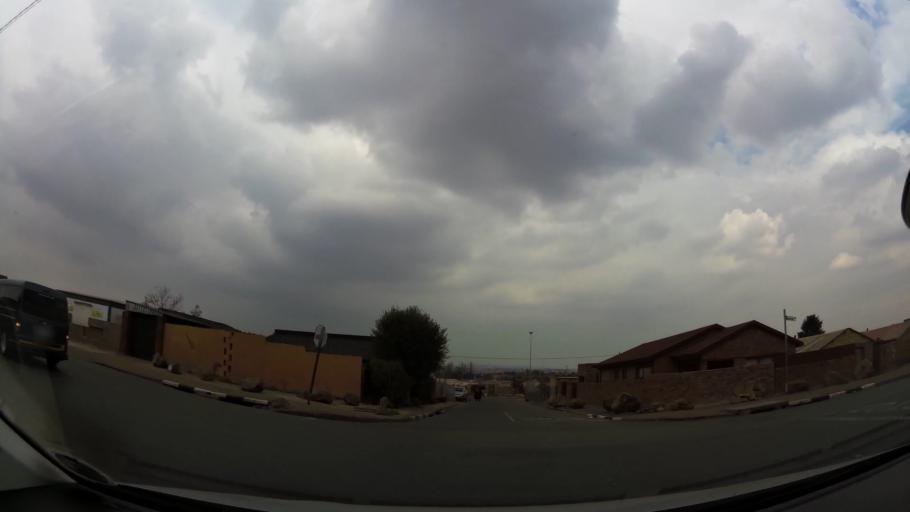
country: ZA
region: Gauteng
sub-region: City of Johannesburg Metropolitan Municipality
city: Soweto
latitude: -26.2631
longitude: 27.8635
